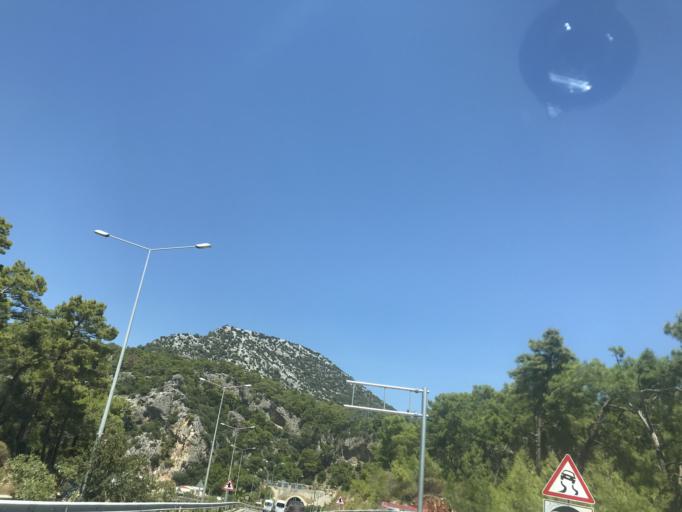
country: TR
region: Antalya
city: Cakirlar
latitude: 36.7591
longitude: 30.5698
